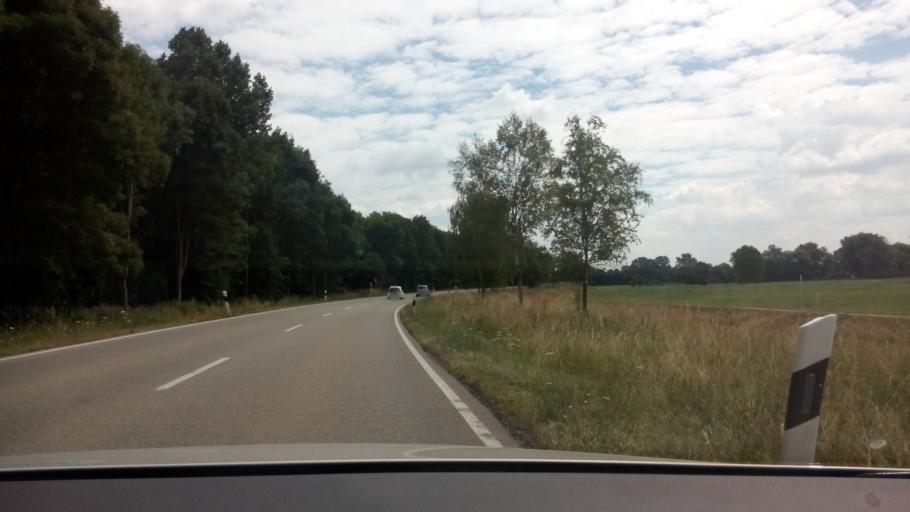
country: DE
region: Bavaria
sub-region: Upper Bavaria
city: Marzling
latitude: 48.3748
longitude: 11.8091
